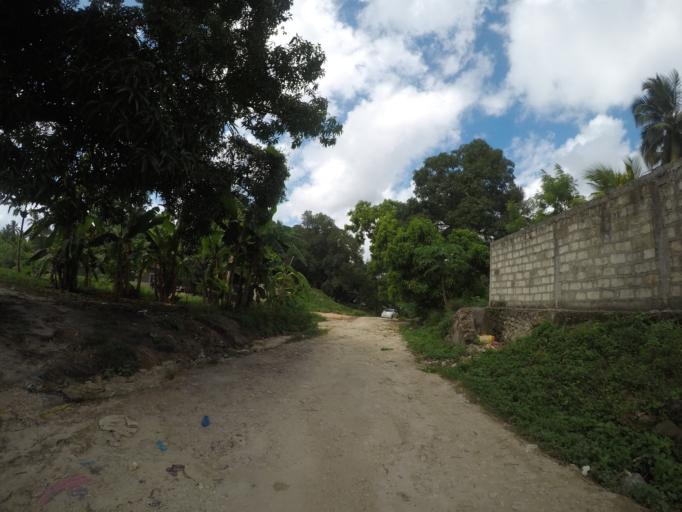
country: TZ
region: Pemba South
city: Chake Chake
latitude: -5.2343
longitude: 39.7795
